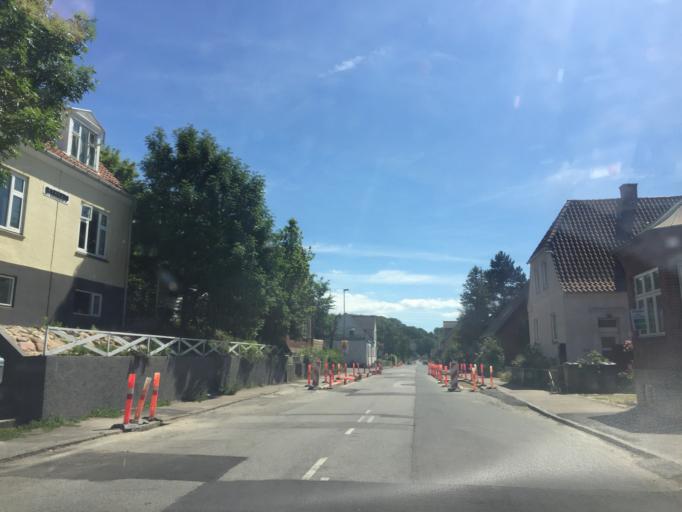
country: DK
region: Capital Region
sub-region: Halsnaes Kommune
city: Frederiksvaerk
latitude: 55.9683
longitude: 12.0205
